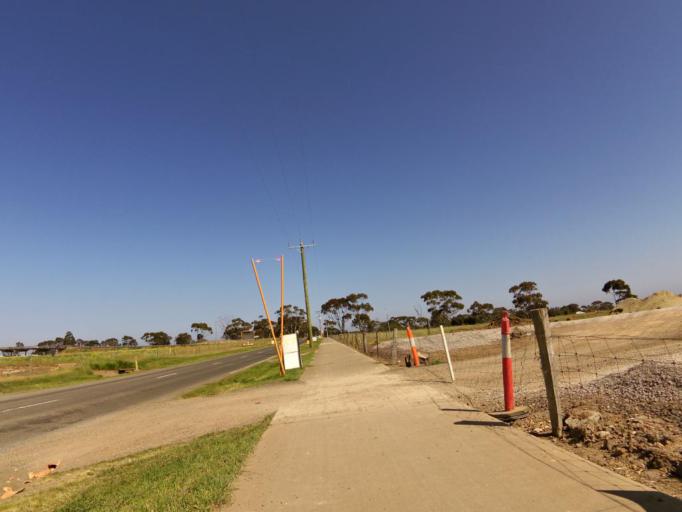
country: AU
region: Victoria
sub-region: Wyndham
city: Hoppers Crossing
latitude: -37.8975
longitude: 144.7013
